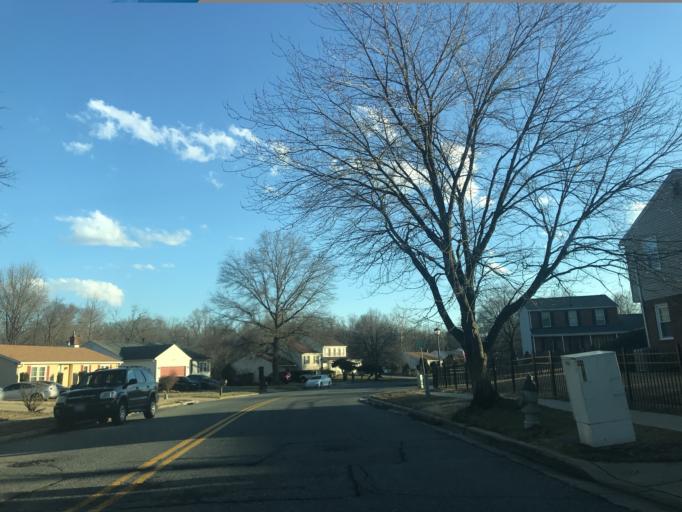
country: US
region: Maryland
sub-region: Prince George's County
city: Woodmore
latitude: 38.9055
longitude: -76.7920
